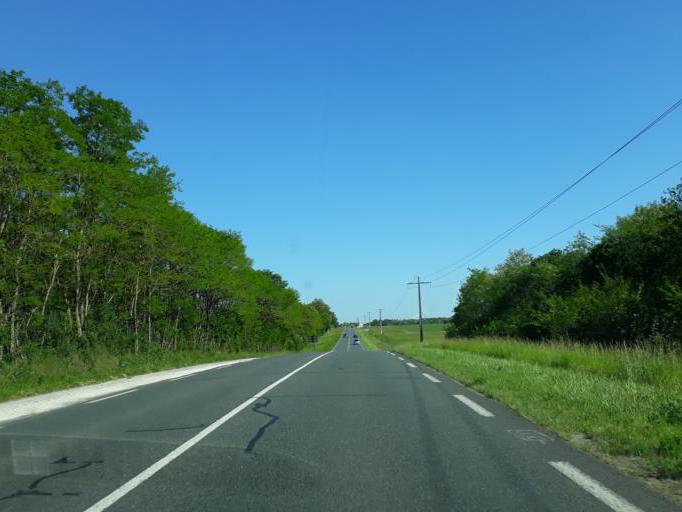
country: FR
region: Centre
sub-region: Departement du Loiret
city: Briare
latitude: 47.6171
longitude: 2.7645
